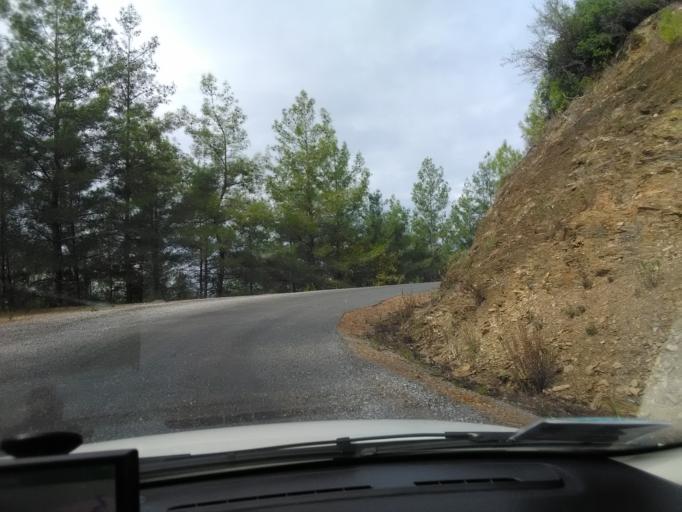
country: TR
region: Antalya
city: Gazipasa
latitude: 36.2426
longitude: 32.4186
